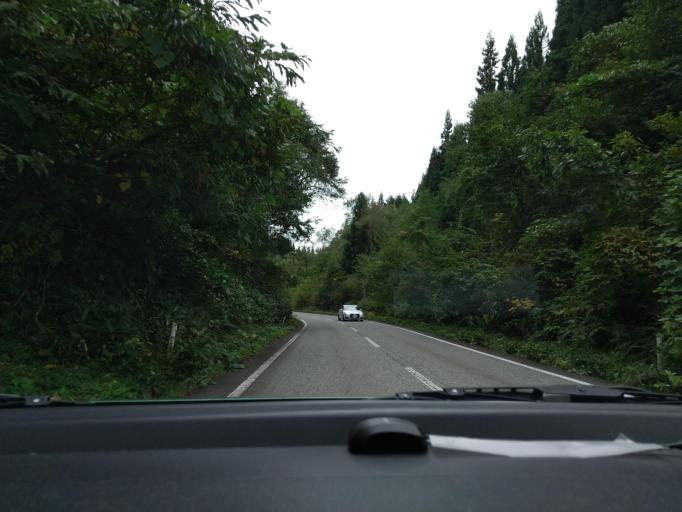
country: JP
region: Akita
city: Kakunodatemachi
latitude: 39.5525
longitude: 140.6332
